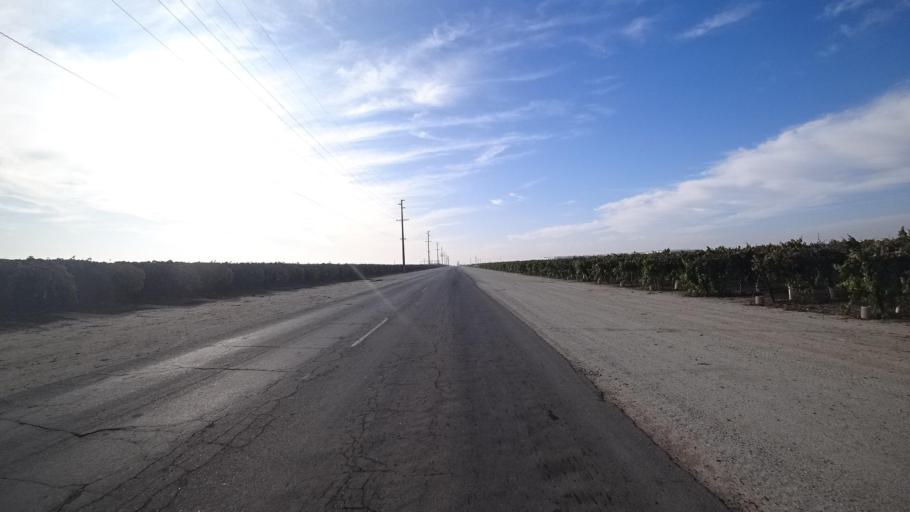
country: US
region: California
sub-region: Kern County
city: McFarland
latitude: 35.7099
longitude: -119.2050
